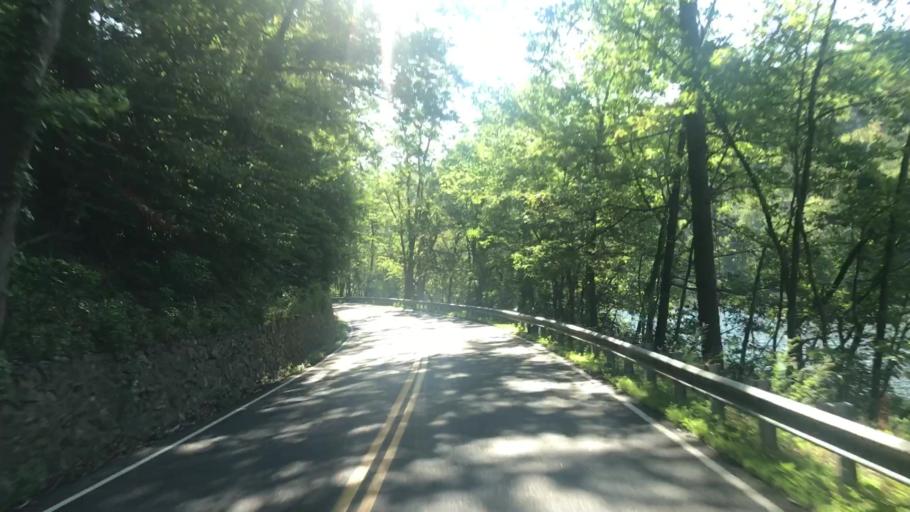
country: US
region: Connecticut
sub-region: Fairfield County
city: Newtown
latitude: 41.4343
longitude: -73.2590
